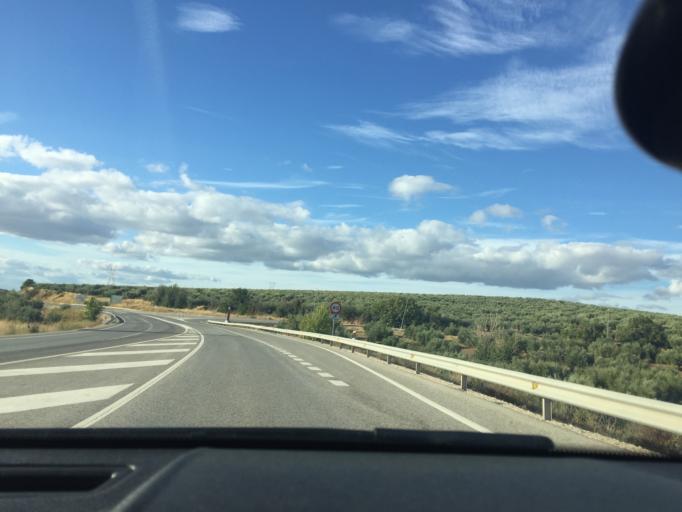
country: ES
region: Andalusia
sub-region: Provincia de Jaen
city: Torredonjimeno
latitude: 37.7687
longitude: -3.9712
